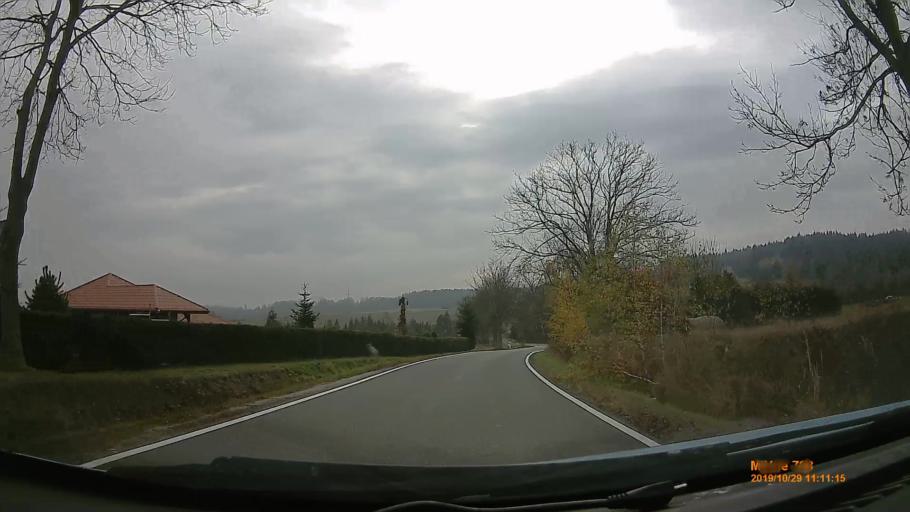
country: PL
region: Lower Silesian Voivodeship
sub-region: Powiat klodzki
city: Polanica-Zdroj
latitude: 50.4365
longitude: 16.5025
